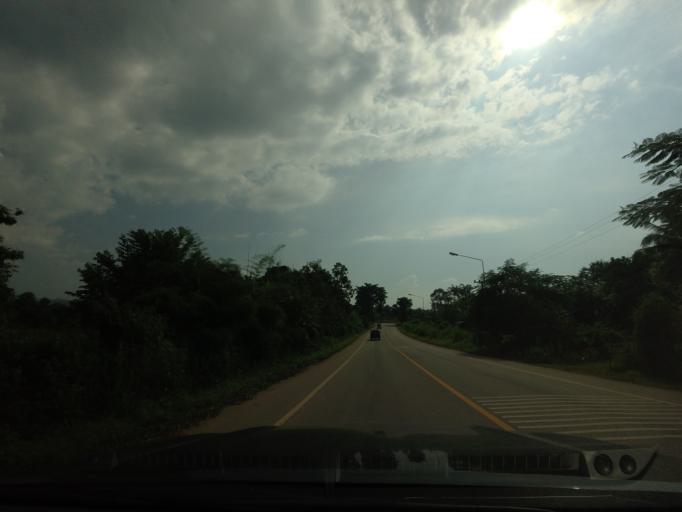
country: TH
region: Phitsanulok
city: Nakhon Thai
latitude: 17.0401
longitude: 100.9134
